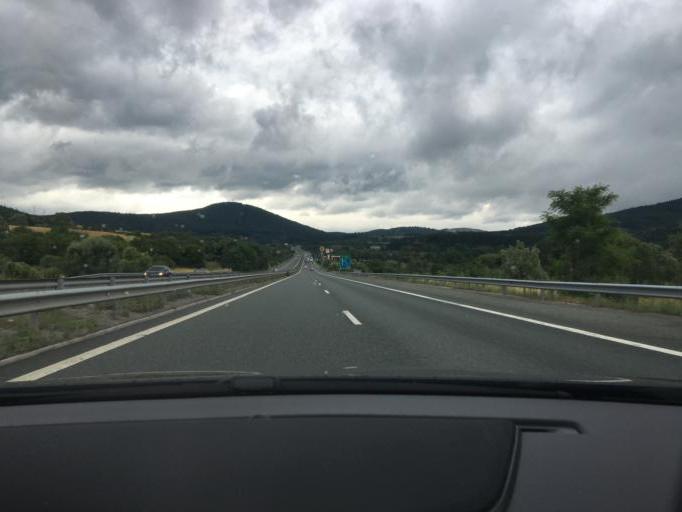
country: BG
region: Pernik
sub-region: Obshtina Pernik
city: Pernik
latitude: 42.5458
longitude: 23.1271
